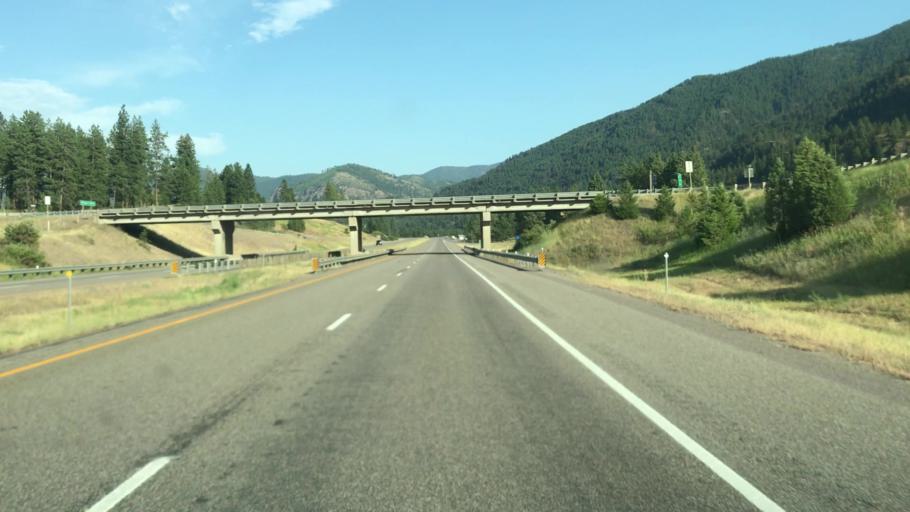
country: US
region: Montana
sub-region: Missoula County
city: Frenchtown
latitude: 47.0065
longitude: -114.4951
